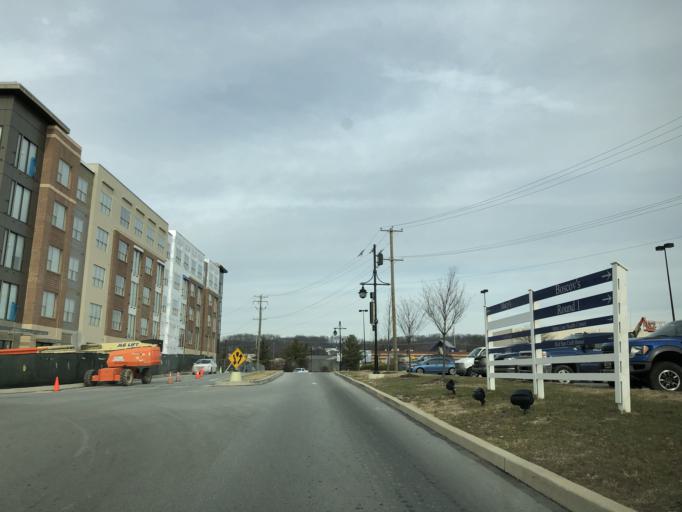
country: US
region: Pennsylvania
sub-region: Chester County
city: Exton
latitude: 40.0313
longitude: -75.6278
